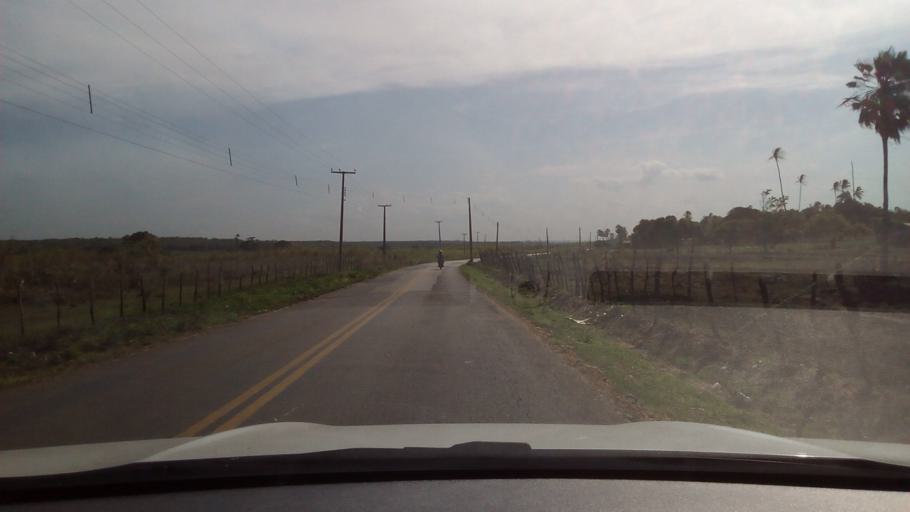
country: BR
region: Rio Grande do Norte
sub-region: Goianinha
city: Goianinha
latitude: -6.2456
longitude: -35.1820
